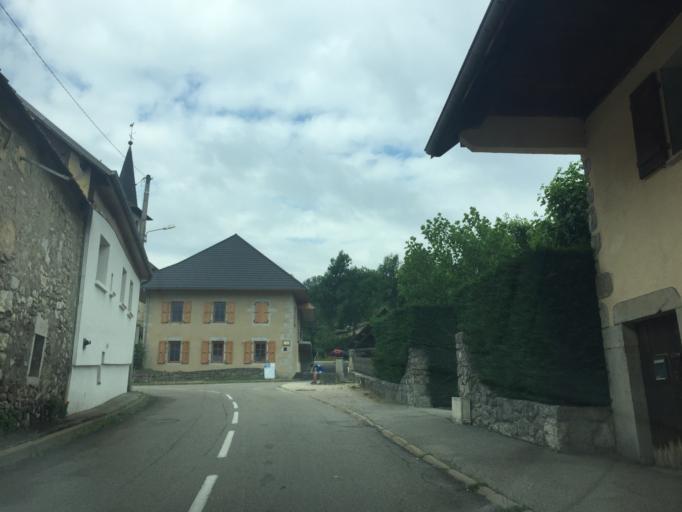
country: FR
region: Rhone-Alpes
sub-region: Departement de la Savoie
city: Barby
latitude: 45.5674
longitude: 6.0087
